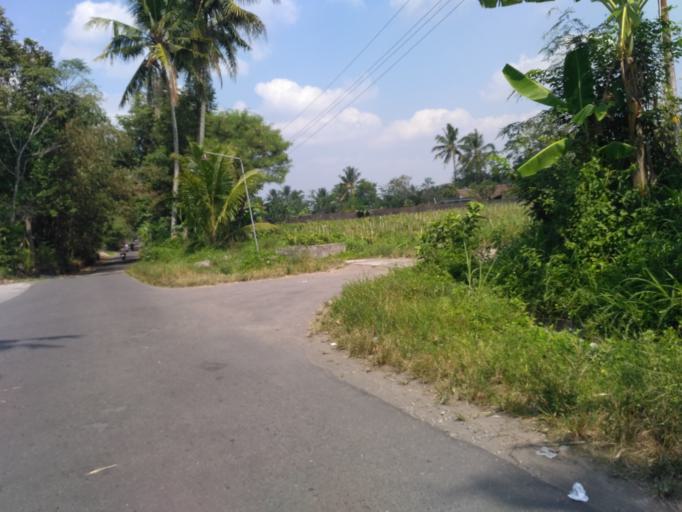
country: ID
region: Daerah Istimewa Yogyakarta
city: Depok
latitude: -7.7151
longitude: 110.4238
